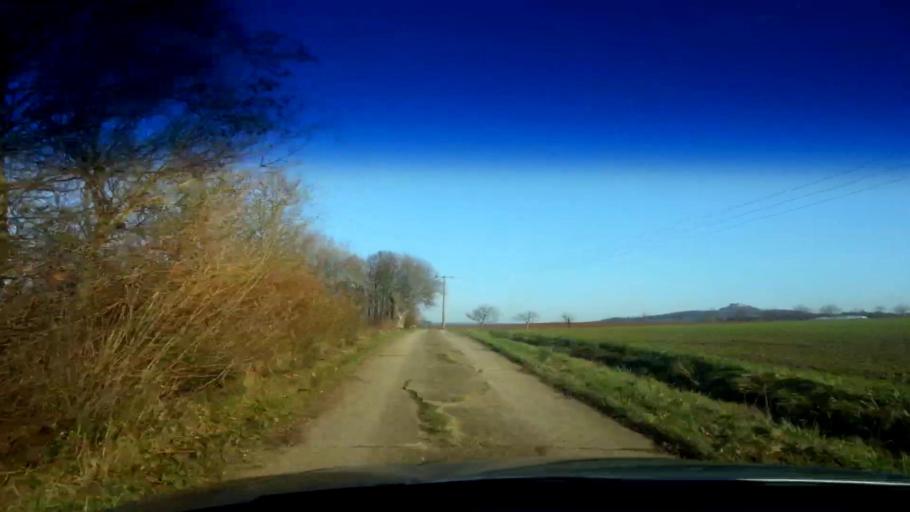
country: DE
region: Bavaria
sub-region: Upper Franconia
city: Litzendorf
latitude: 49.9438
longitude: 11.0007
